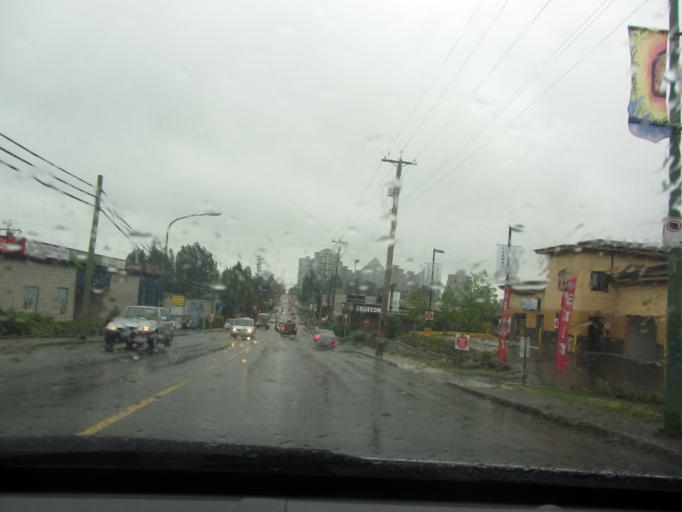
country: CA
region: British Columbia
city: New Westminster
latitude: 49.2201
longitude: -122.9291
